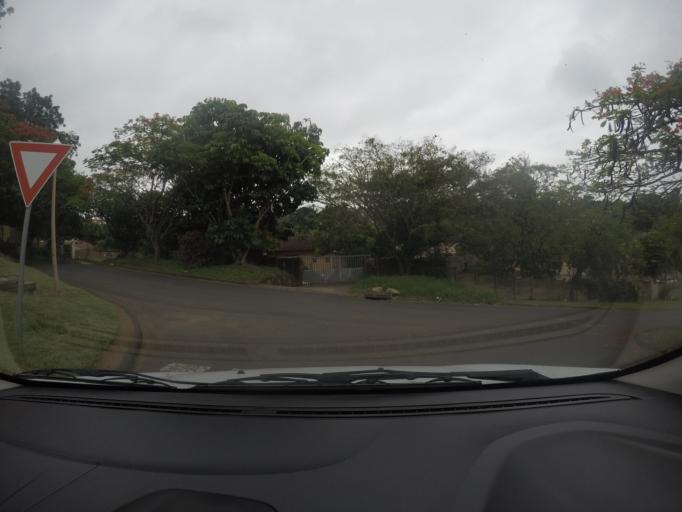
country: ZA
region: KwaZulu-Natal
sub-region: uThungulu District Municipality
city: Empangeni
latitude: -28.7580
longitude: 31.8850
